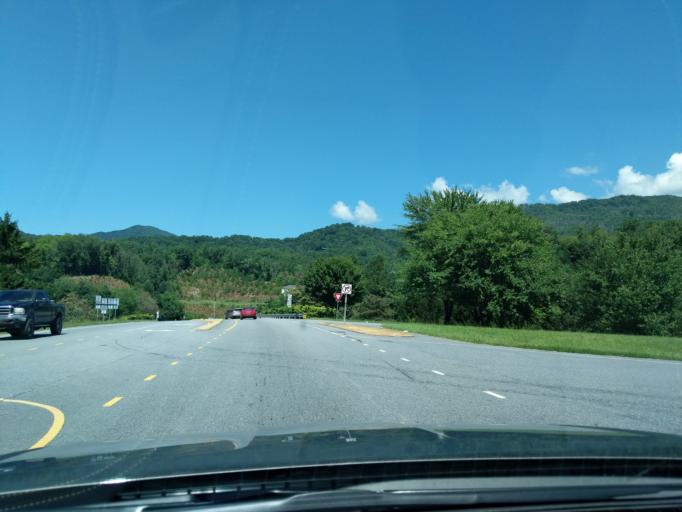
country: US
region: North Carolina
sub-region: Jackson County
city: Sylva
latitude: 35.3773
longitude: -83.2555
